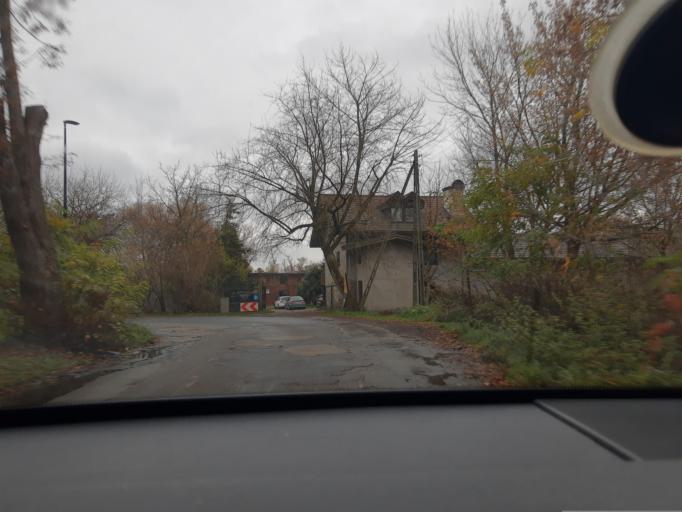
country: PL
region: Lodz Voivodeship
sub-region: Powiat pabianicki
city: Konstantynow Lodzki
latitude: 51.7438
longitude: 19.3713
